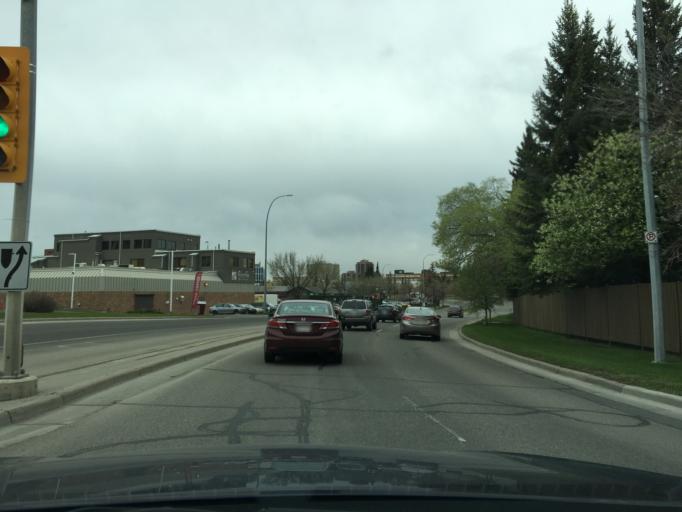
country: CA
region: Alberta
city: Calgary
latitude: 50.9551
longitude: -114.0679
